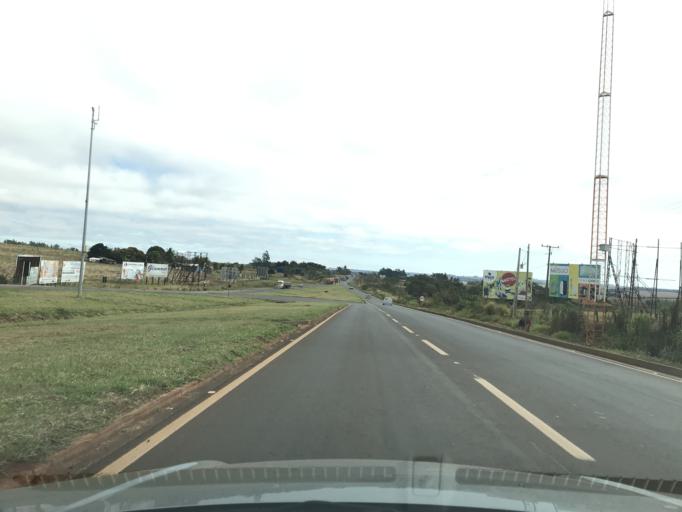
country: PY
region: Canindeyu
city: Salto del Guaira
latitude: -24.0014
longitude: -54.3191
